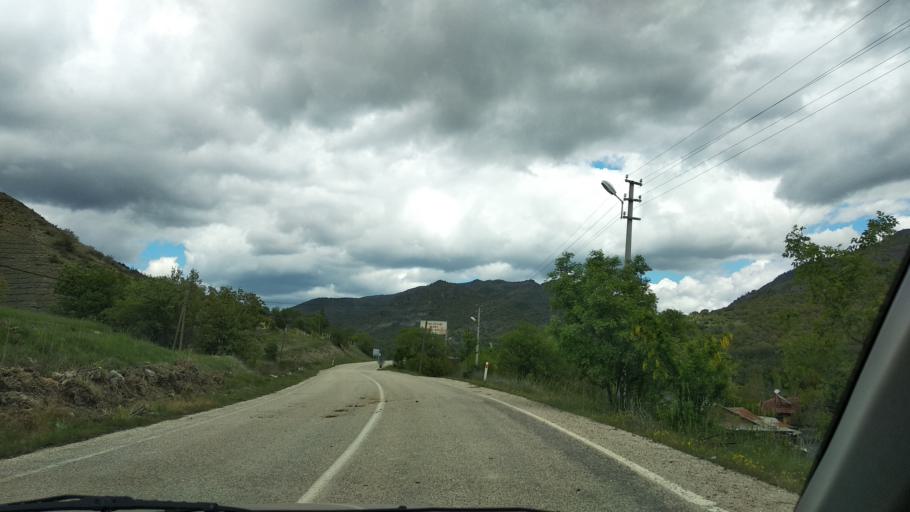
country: TR
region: Bolu
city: Seben
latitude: 40.4200
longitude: 31.5840
